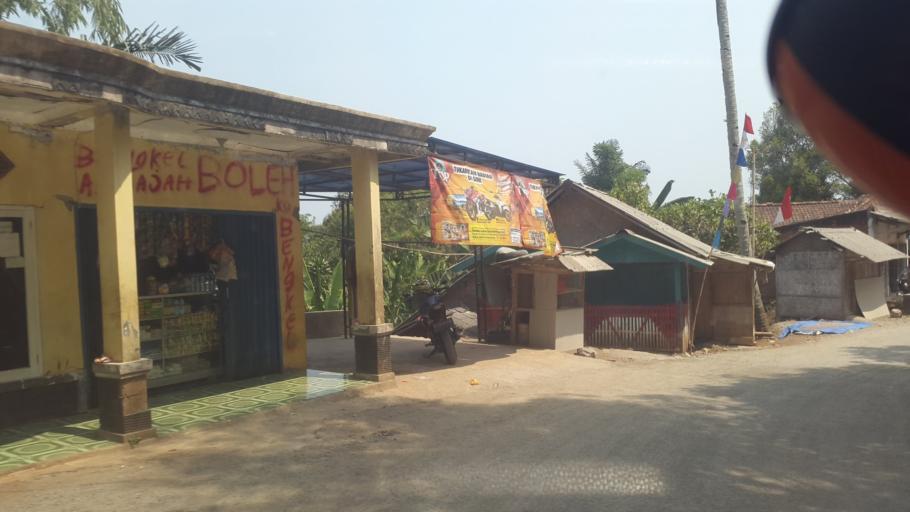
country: ID
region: West Java
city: Nagrak
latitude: -6.9017
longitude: 106.5230
